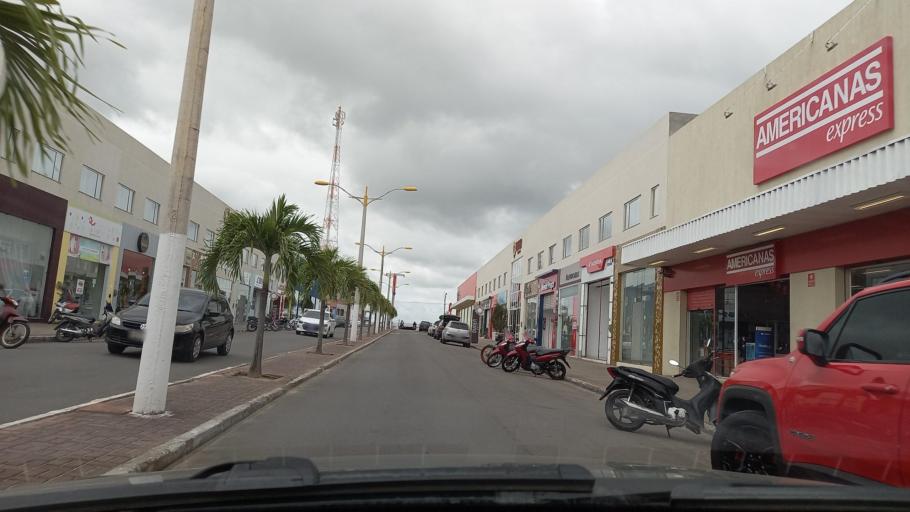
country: BR
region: Sergipe
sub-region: Caninde De Sao Francisco
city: Caninde de Sao Francisco
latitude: -9.6093
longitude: -37.7631
